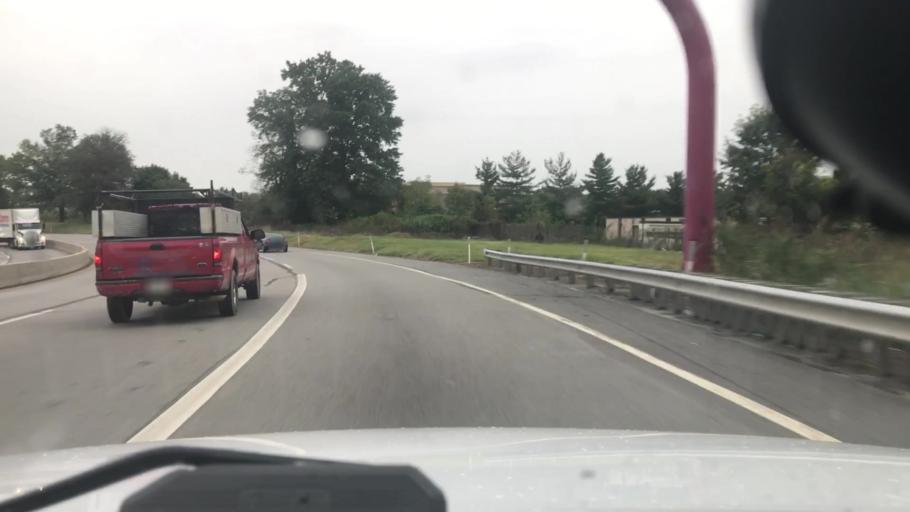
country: US
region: Pennsylvania
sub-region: Montgomery County
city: Fort Washington
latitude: 40.1344
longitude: -75.1934
